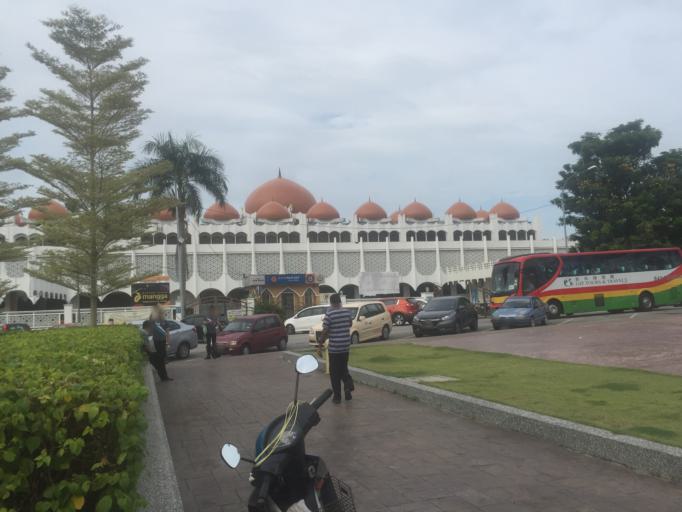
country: MY
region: Perak
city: Ipoh
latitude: 4.5968
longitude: 101.0761
